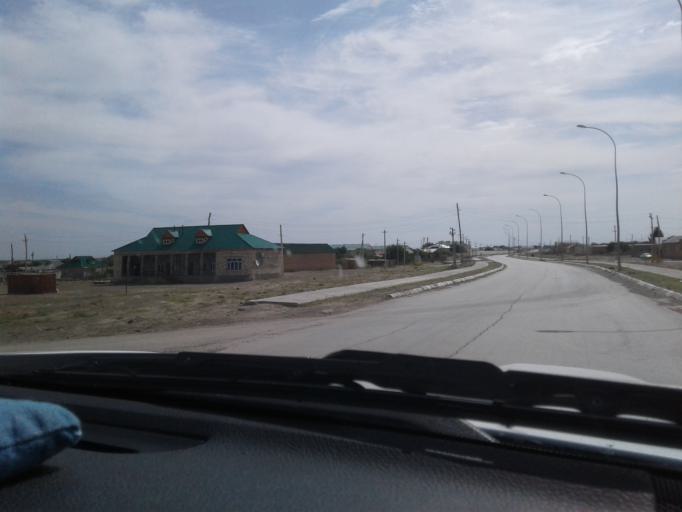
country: TM
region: Balkan
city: Gazanjyk
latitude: 39.2453
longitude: 55.4870
